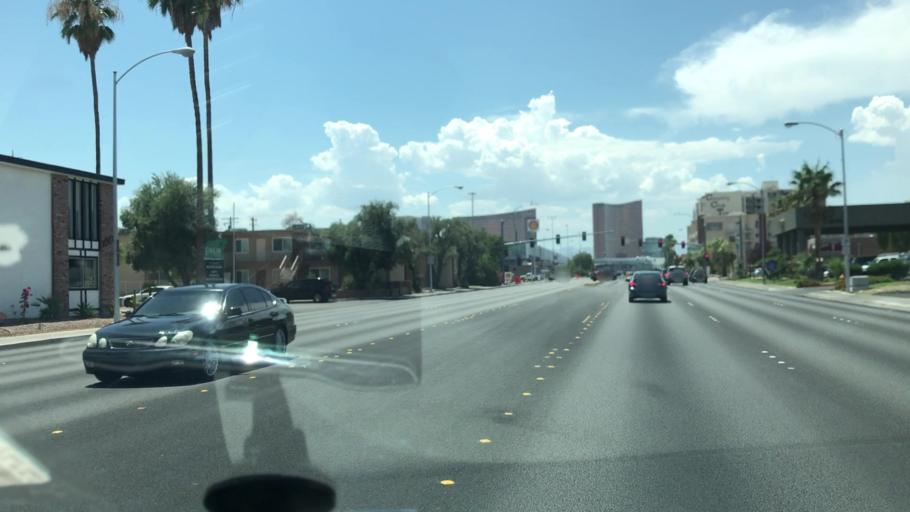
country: US
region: Nevada
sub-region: Clark County
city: Winchester
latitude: 36.1298
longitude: -115.1399
